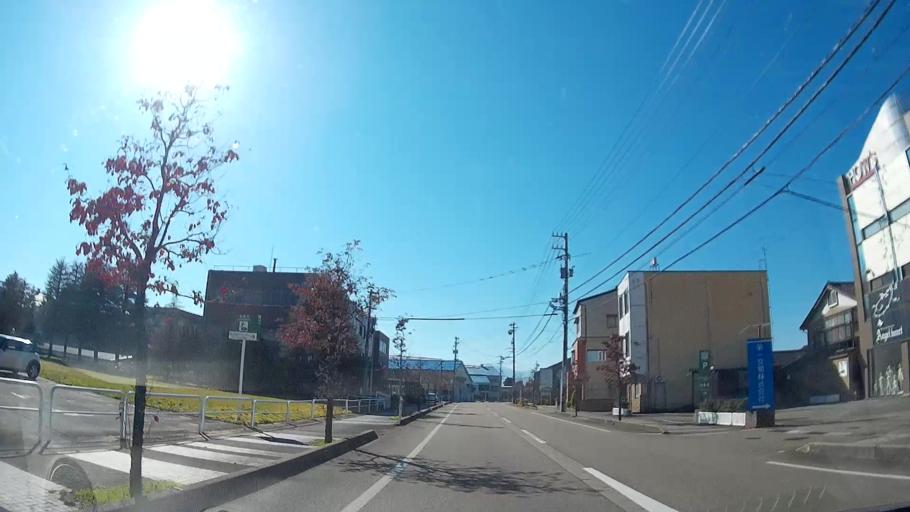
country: JP
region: Toyama
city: Nanto-shi
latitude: 36.5876
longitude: 136.9187
